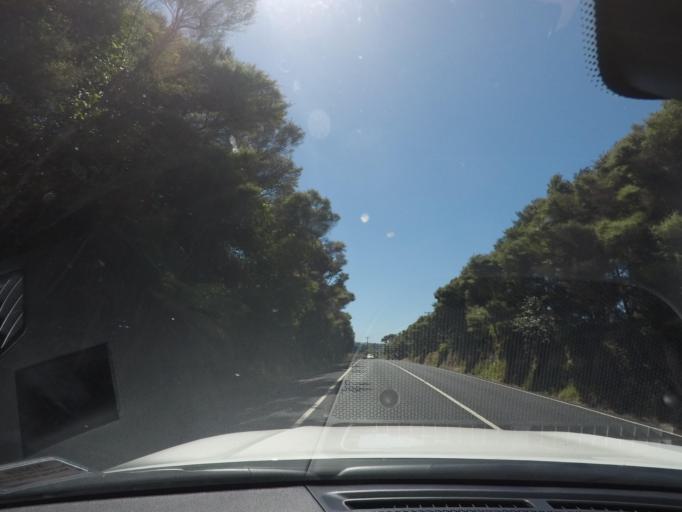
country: NZ
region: Auckland
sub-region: Auckland
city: Parakai
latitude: -36.6262
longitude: 174.3607
